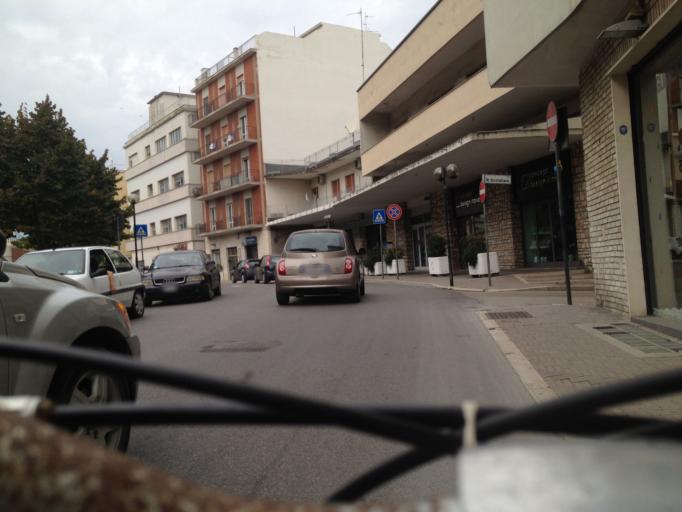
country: IT
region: Basilicate
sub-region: Provincia di Matera
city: Matera
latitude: 40.6647
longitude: 16.6076
